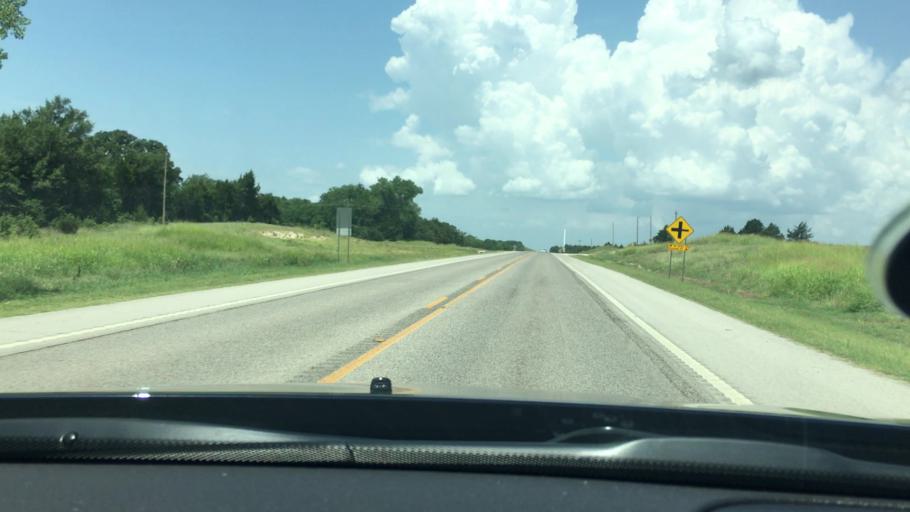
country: US
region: Oklahoma
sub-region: Carter County
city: Dickson
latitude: 34.1003
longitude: -96.9311
